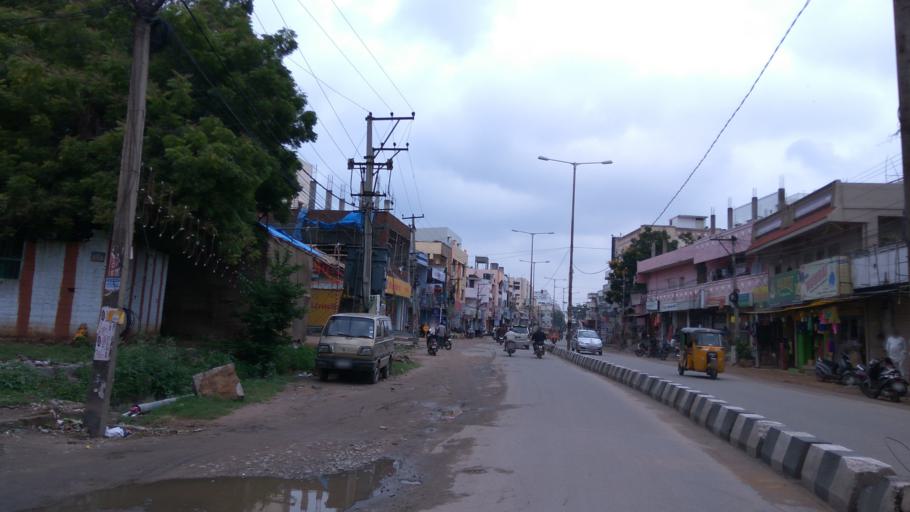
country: IN
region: Telangana
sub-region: Hyderabad
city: Malkajgiri
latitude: 17.4542
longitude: 78.5346
